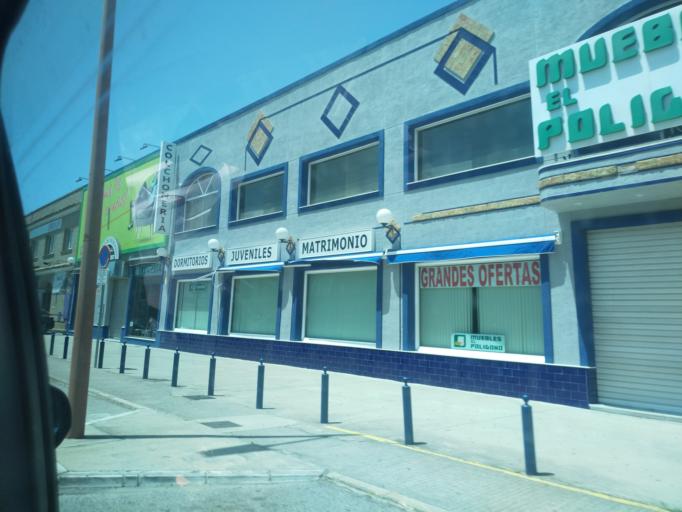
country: ES
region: Andalusia
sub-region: Provincia de Cadiz
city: Chiclana de la Frontera
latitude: 36.4303
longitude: -6.1471
